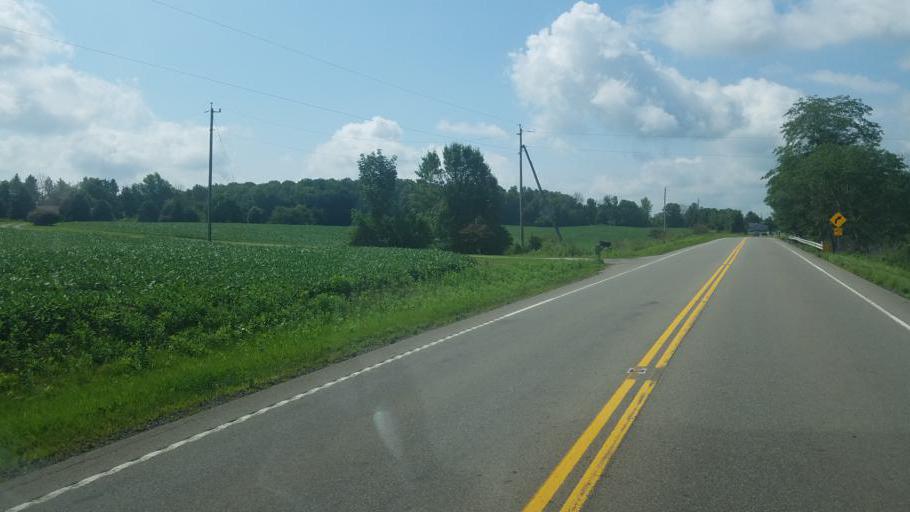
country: US
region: Ohio
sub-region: Licking County
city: Hebron
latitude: 39.9724
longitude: -82.5267
